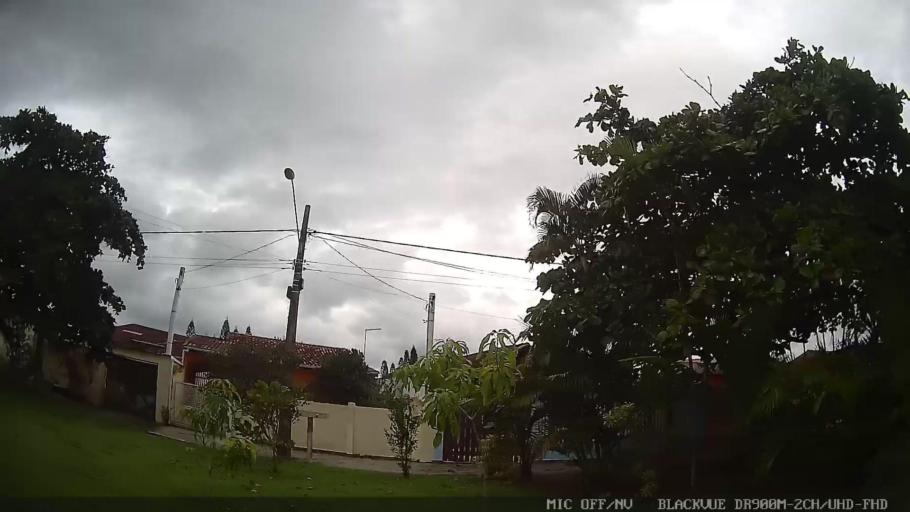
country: BR
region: Sao Paulo
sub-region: Itanhaem
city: Itanhaem
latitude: -24.1536
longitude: -46.7313
